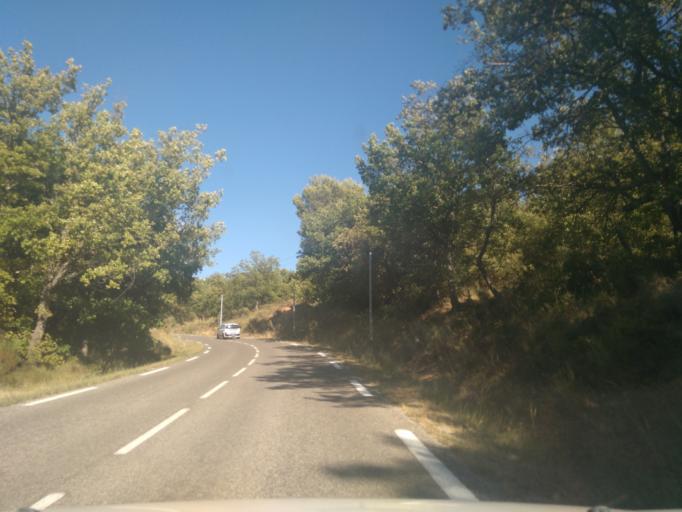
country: FR
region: Provence-Alpes-Cote d'Azur
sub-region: Departement du Var
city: Regusse
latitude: 43.7258
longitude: 6.1529
